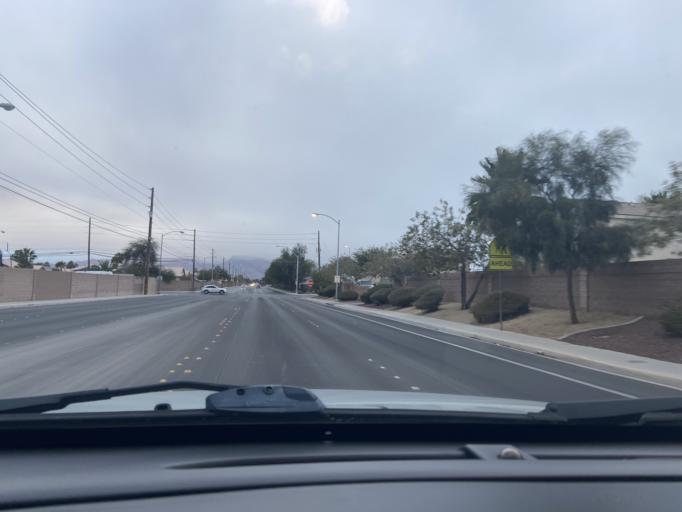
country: US
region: Nevada
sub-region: Clark County
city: Las Vegas
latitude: 36.2248
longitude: -115.1877
